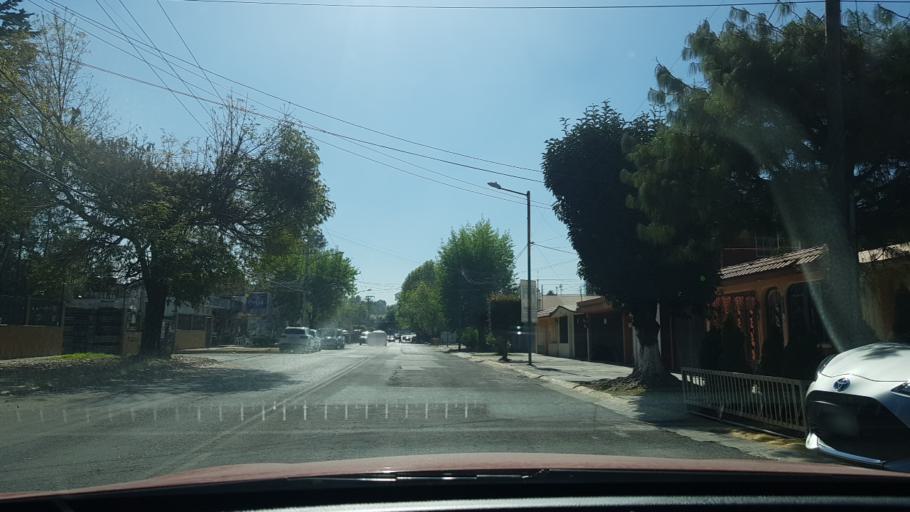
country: MX
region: Mexico
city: Cuautitlan Izcalli
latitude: 19.6491
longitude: -99.2019
